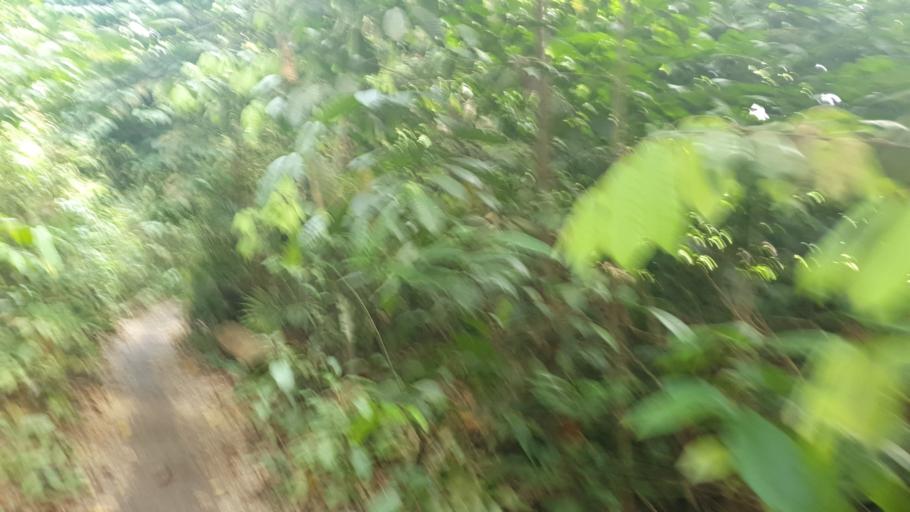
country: SG
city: Singapore
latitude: 1.3400
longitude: 103.8159
